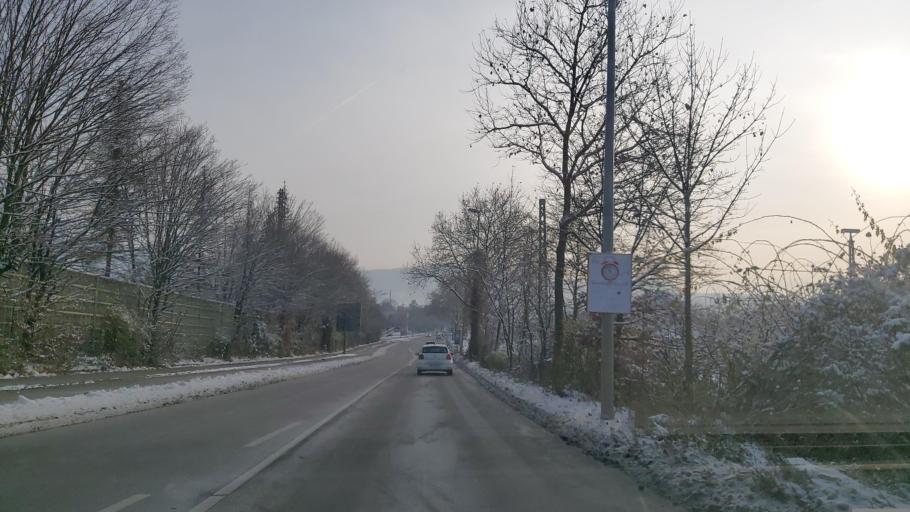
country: DE
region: Baden-Wuerttemberg
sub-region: Tuebingen Region
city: Metzingen
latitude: 48.5422
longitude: 9.2901
